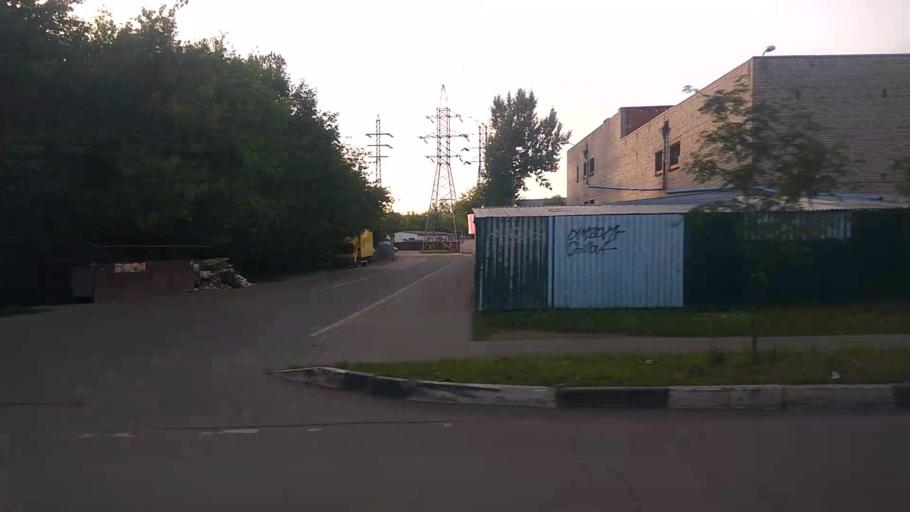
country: RU
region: Moskovskaya
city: Korolev
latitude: 55.9188
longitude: 37.7810
